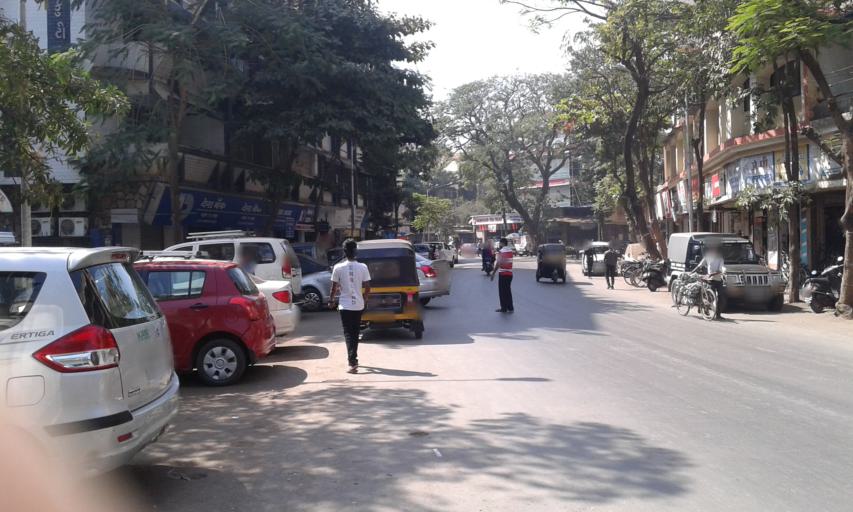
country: IN
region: Maharashtra
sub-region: Thane
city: Bhayandar
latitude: 19.3028
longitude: 72.8495
